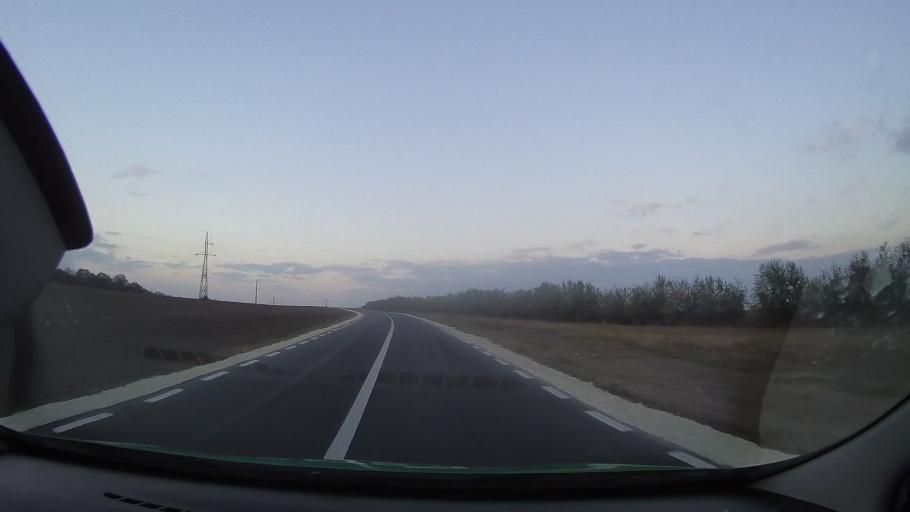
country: RO
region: Constanta
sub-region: Comuna Baneasa
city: Baneasa
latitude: 44.1077
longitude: 27.6707
